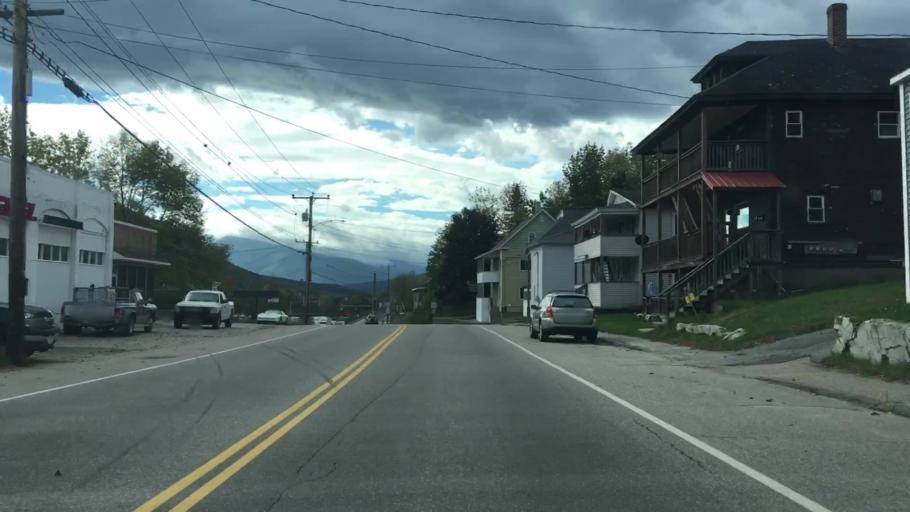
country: US
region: New Hampshire
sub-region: Coos County
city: Berlin
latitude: 44.4626
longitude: -71.1867
